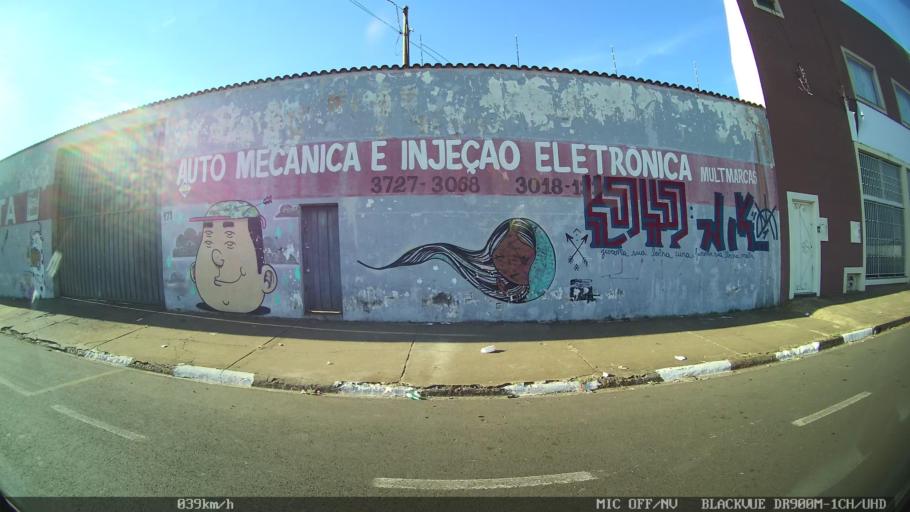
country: BR
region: Sao Paulo
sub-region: Franca
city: Franca
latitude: -20.5145
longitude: -47.3740
